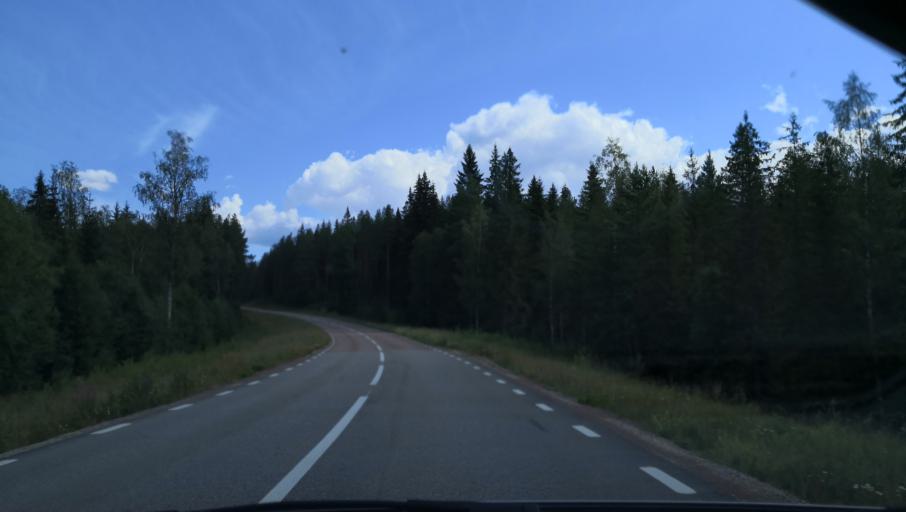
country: SE
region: Dalarna
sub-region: Rattviks Kommun
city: Vikarbyn
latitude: 61.1625
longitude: 15.0155
